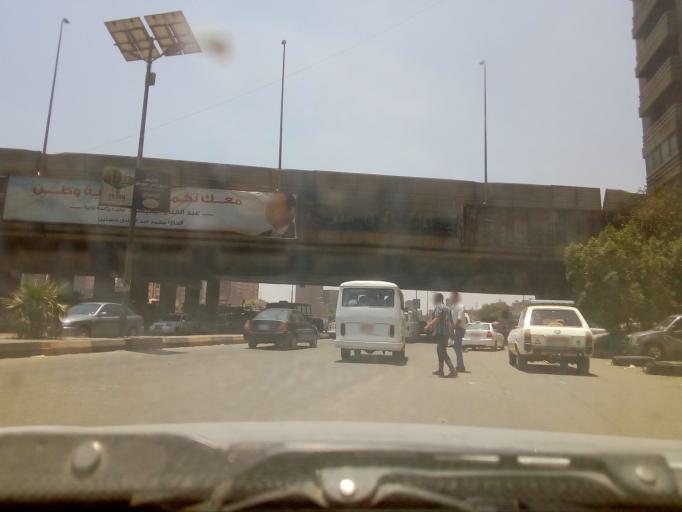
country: EG
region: Al Jizah
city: Al Jizah
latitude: 29.9872
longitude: 31.2142
